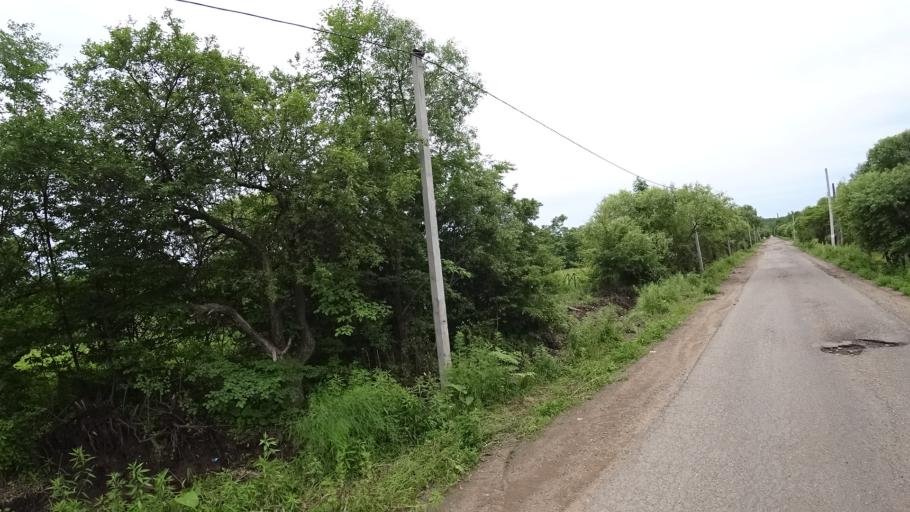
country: RU
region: Primorskiy
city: Novosysoyevka
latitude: 44.2079
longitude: 133.3322
